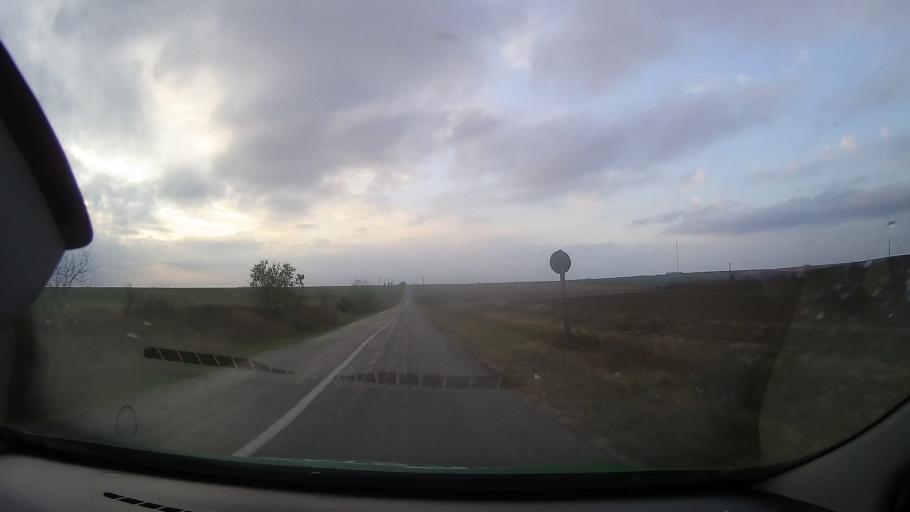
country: RO
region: Constanta
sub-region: Comuna Dobromir
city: Dobromir
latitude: 44.0326
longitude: 27.7697
